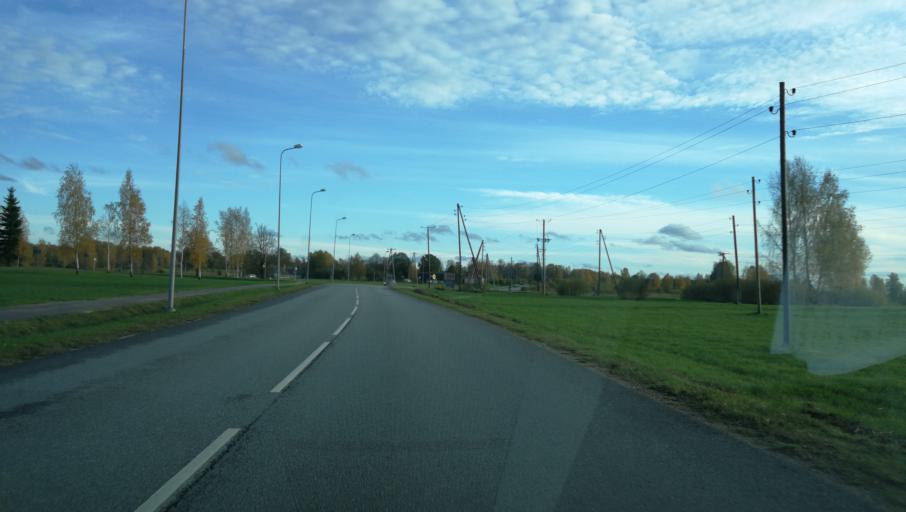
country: LV
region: Cesu Rajons
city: Cesis
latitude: 57.3021
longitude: 25.2434
